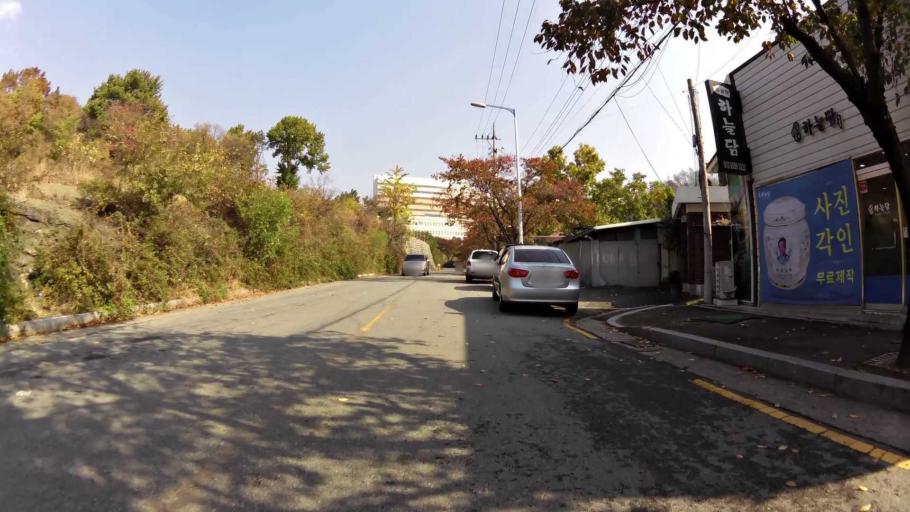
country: KR
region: Daegu
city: Daegu
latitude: 35.8547
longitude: 128.6573
